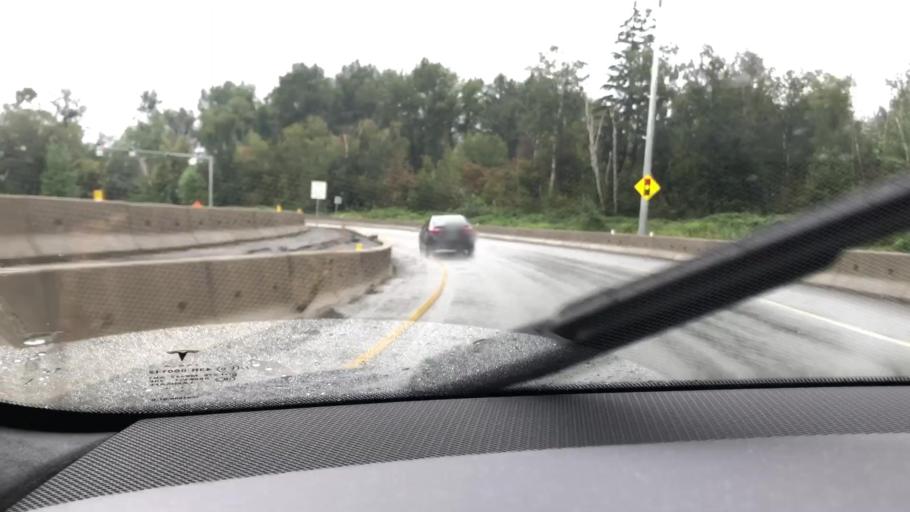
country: CA
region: British Columbia
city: Burnaby
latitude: 49.2457
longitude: -122.9629
